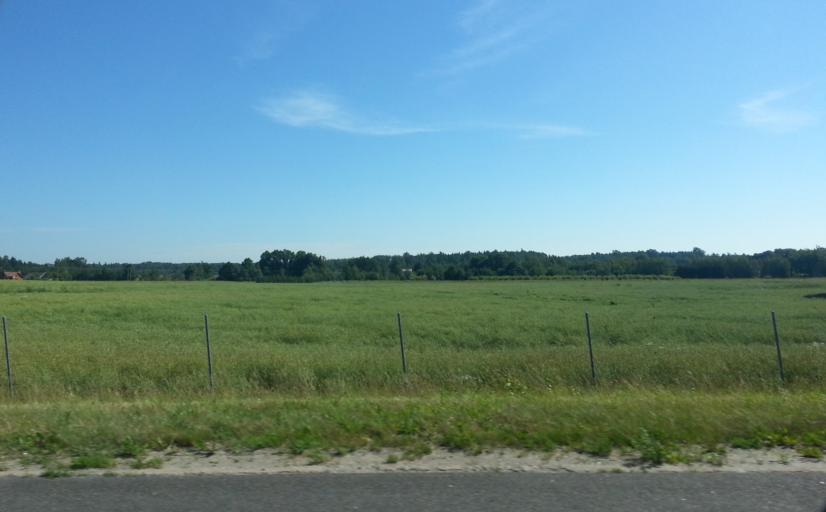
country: LT
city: Sirvintos
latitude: 55.0849
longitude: 24.8712
